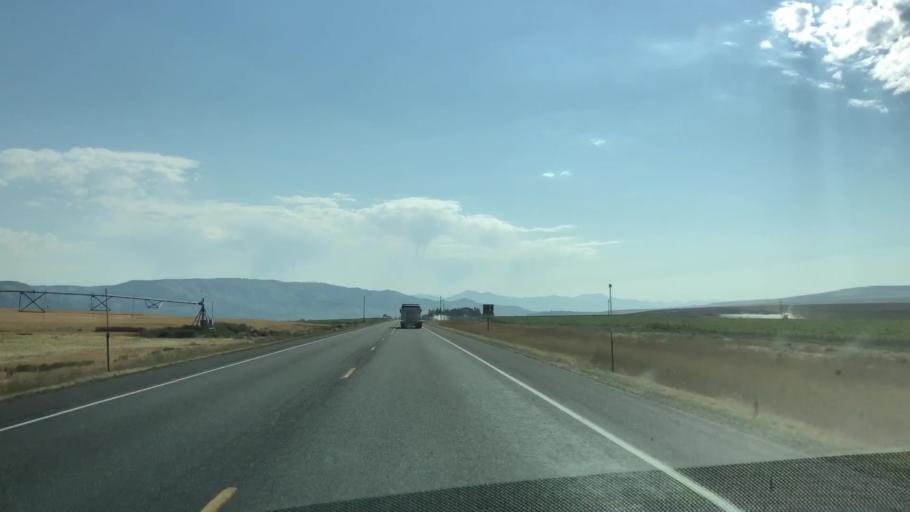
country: US
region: Idaho
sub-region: Jefferson County
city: Rigby
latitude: 43.6140
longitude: -111.7521
